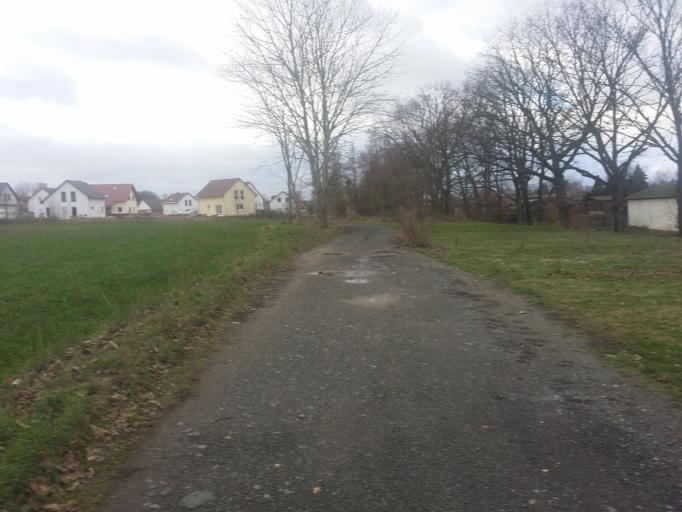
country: DE
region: Saxony
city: Otterwisch
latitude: 51.2408
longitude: 12.6208
